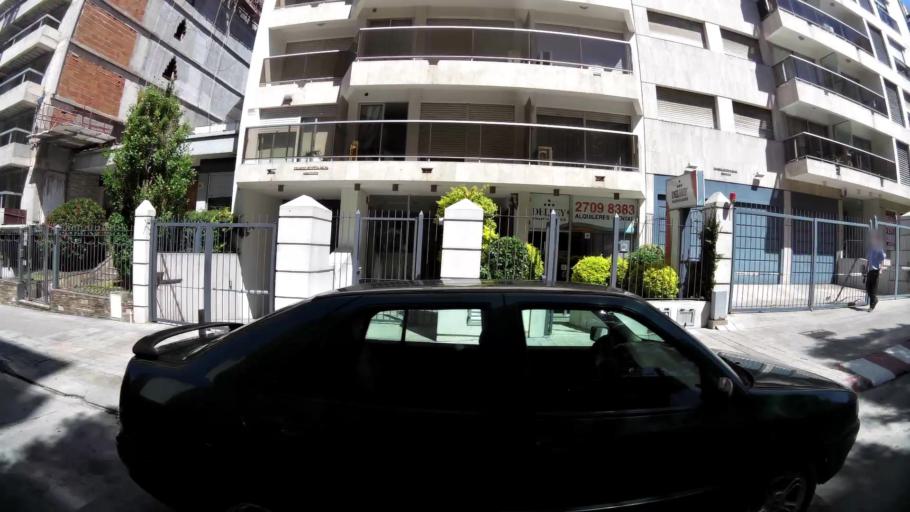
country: UY
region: Montevideo
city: Montevideo
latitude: -34.9084
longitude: -56.1471
